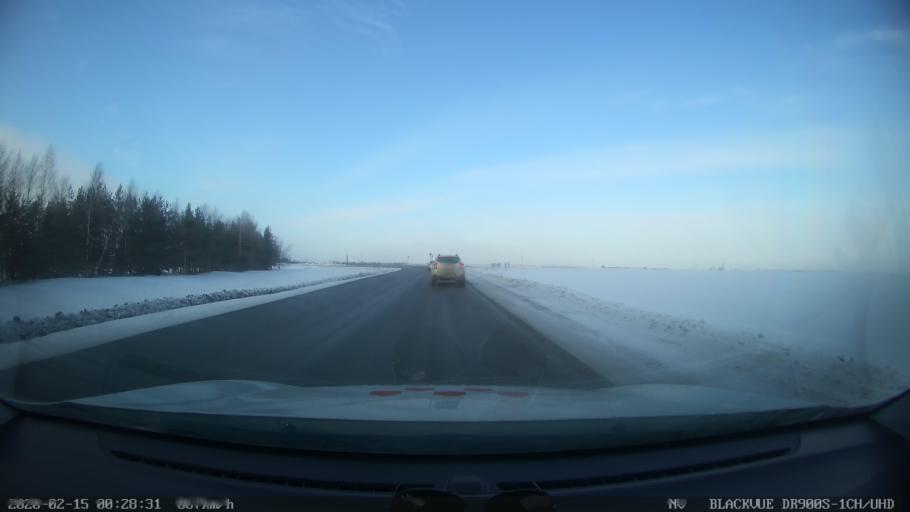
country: RU
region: Tatarstan
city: Verkhniy Uslon
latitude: 55.6431
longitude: 48.8761
